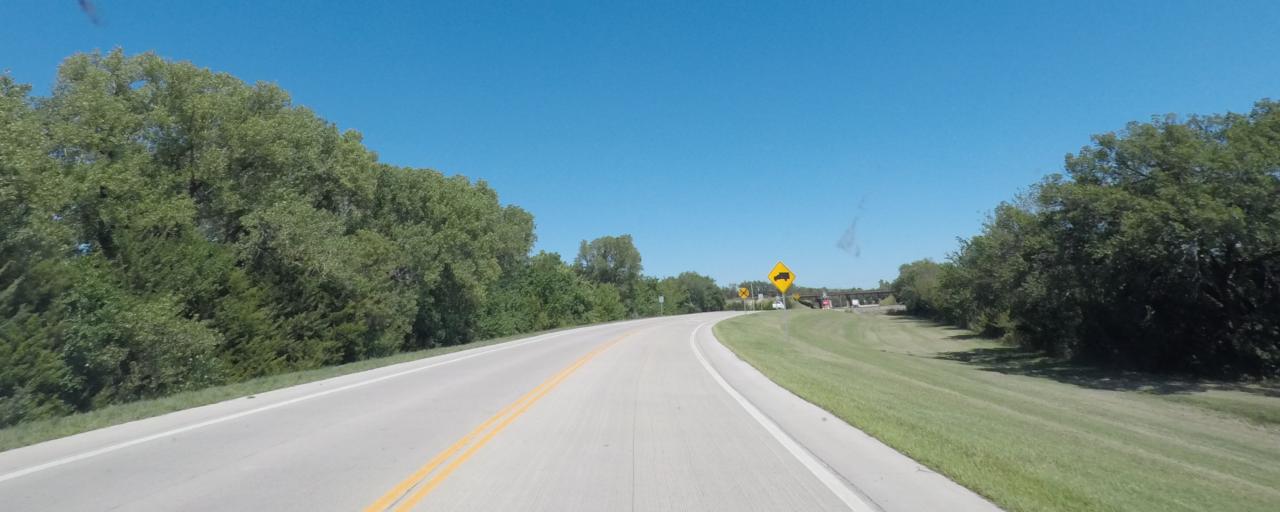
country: US
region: Kansas
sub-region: Sumner County
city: Wellington
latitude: 37.2580
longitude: -97.4067
